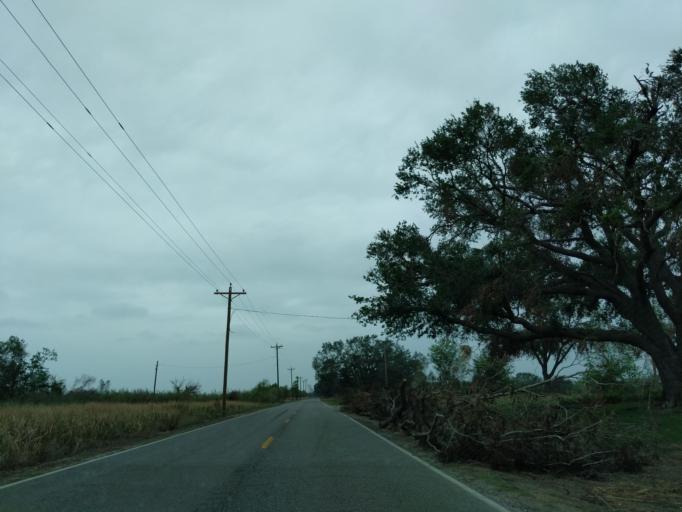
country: US
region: Louisiana
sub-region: Jefferson Davis Parish
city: Lake Arthur
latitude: 29.7534
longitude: -92.9146
